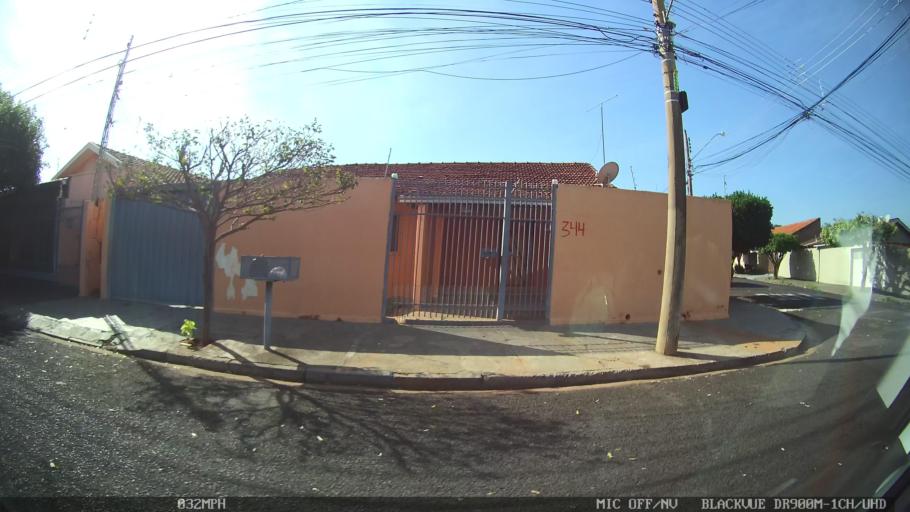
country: BR
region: Sao Paulo
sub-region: Sao Jose Do Rio Preto
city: Sao Jose do Rio Preto
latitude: -20.7897
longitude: -49.4087
